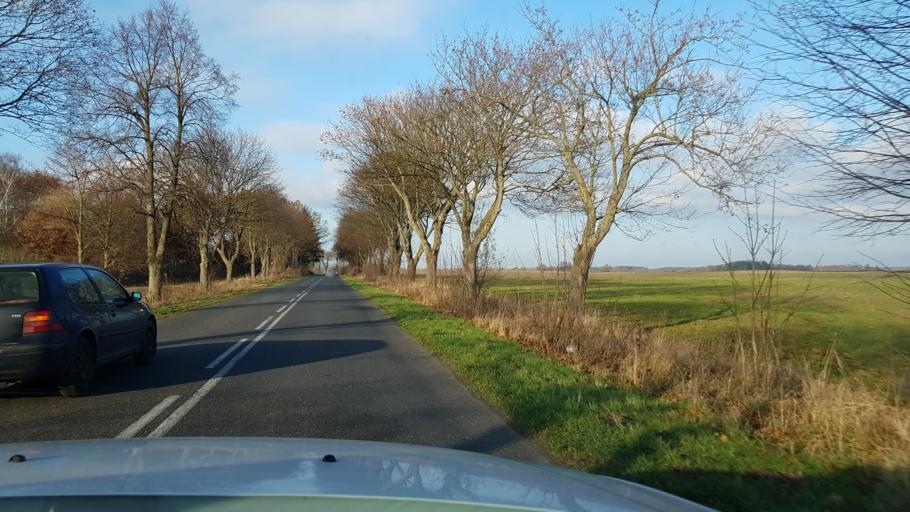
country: PL
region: West Pomeranian Voivodeship
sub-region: Powiat stargardzki
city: Chociwel
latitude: 53.4479
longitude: 15.3481
